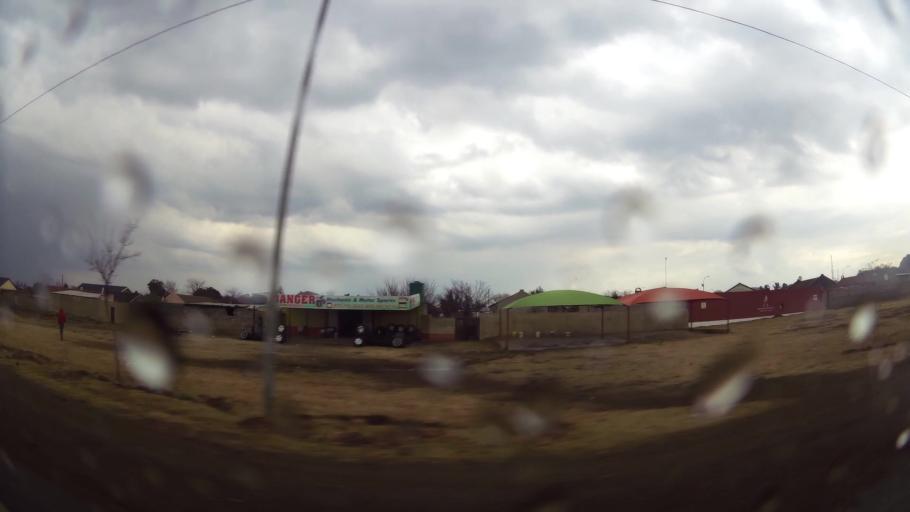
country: ZA
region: Gauteng
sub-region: Ekurhuleni Metropolitan Municipality
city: Germiston
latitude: -26.3757
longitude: 28.1341
